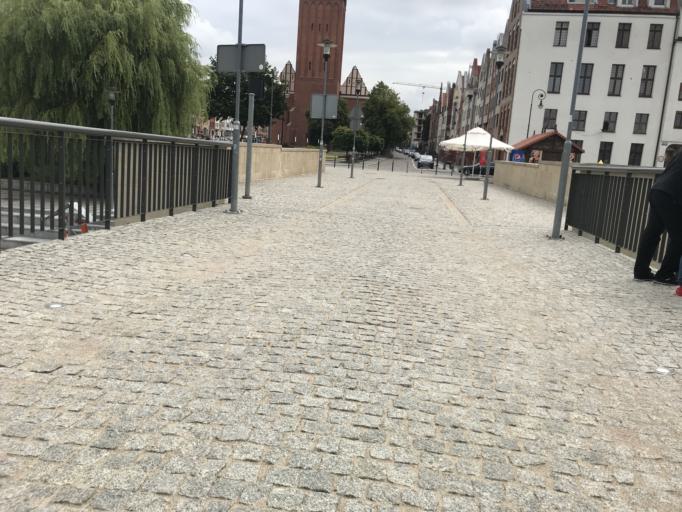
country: PL
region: Warmian-Masurian Voivodeship
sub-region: Powiat elblaski
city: Elblag
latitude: 54.1580
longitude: 19.3923
